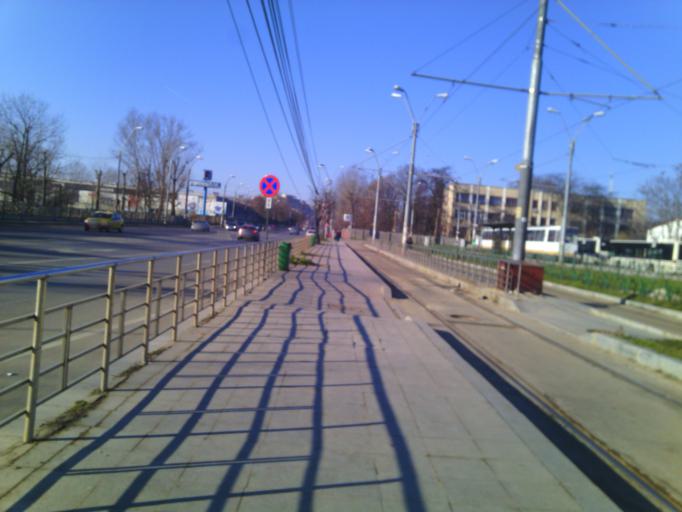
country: RO
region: Ilfov
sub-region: Comuna Popesti-Leordeni
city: Popesti-Leordeni
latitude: 44.3835
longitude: 26.1463
